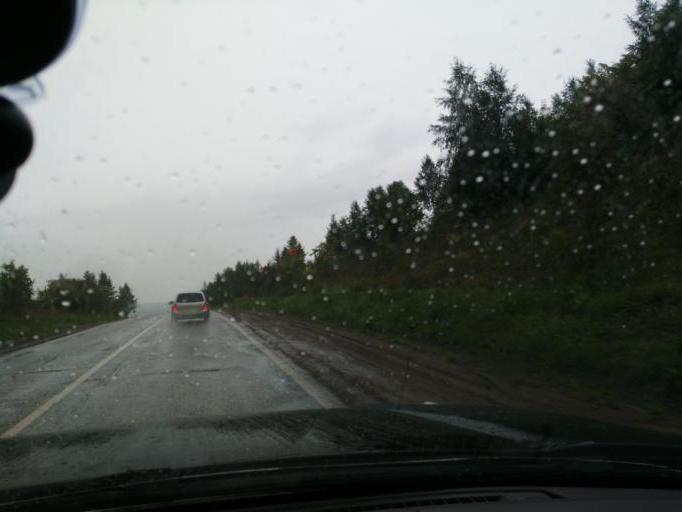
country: RU
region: Perm
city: Barda
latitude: 56.9179
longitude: 55.6805
